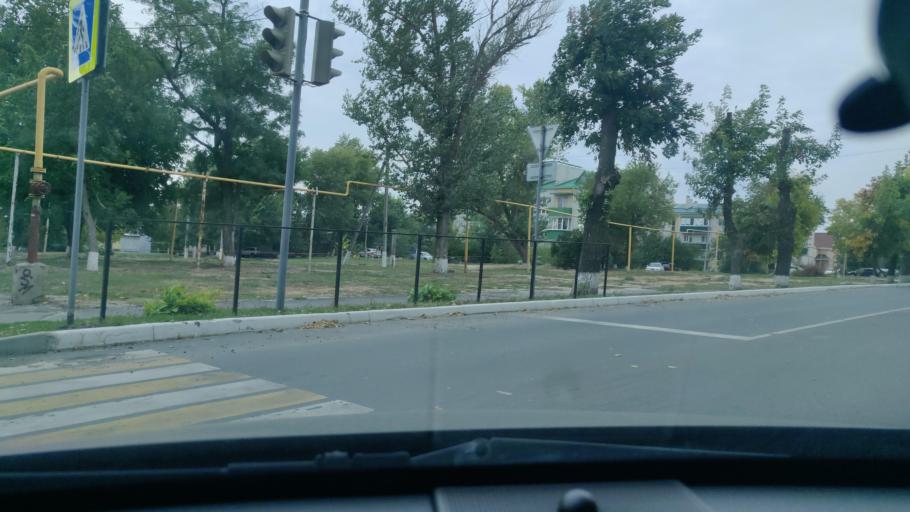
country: RU
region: Rostov
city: Ust'-Donetskiy
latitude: 47.6415
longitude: 40.8732
